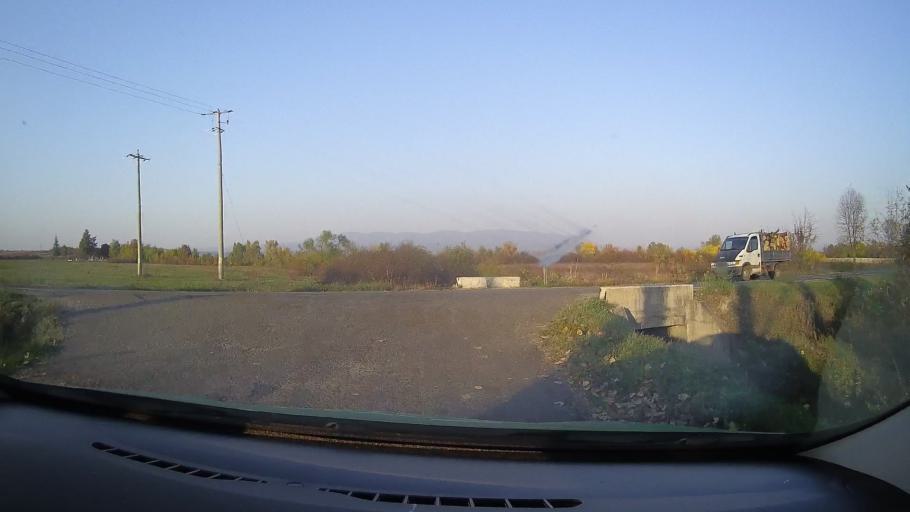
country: RO
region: Arad
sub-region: Comuna Barsa
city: Barsa
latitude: 46.3861
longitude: 22.0657
